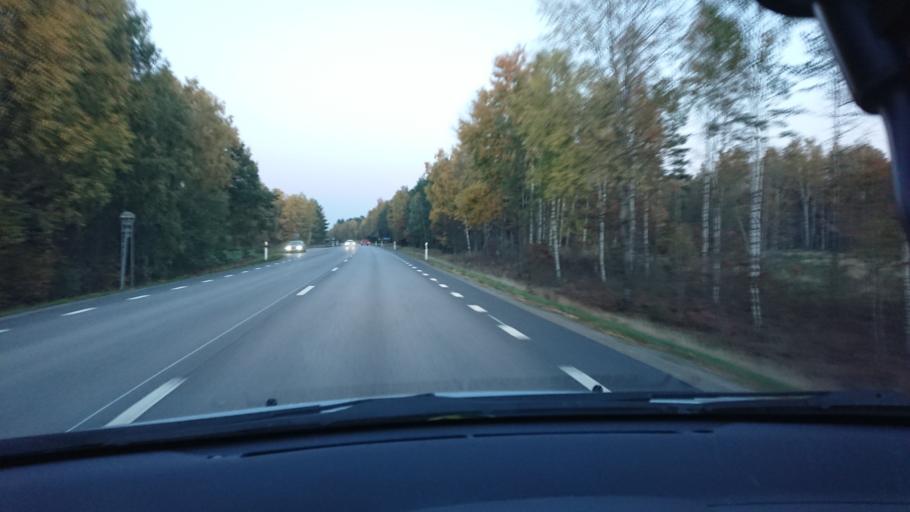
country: SE
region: Kronoberg
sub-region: Markaryds Kommun
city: Stromsnasbruk
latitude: 56.7560
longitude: 13.7474
